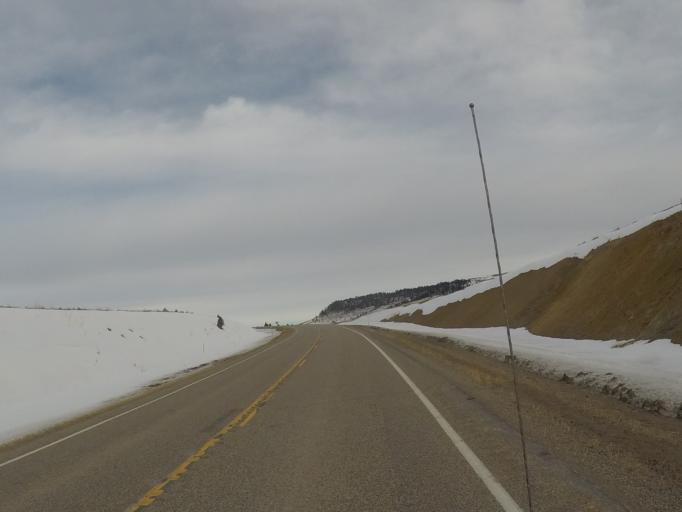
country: US
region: Montana
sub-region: Meagher County
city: White Sulphur Springs
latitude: 46.6373
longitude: -110.8718
